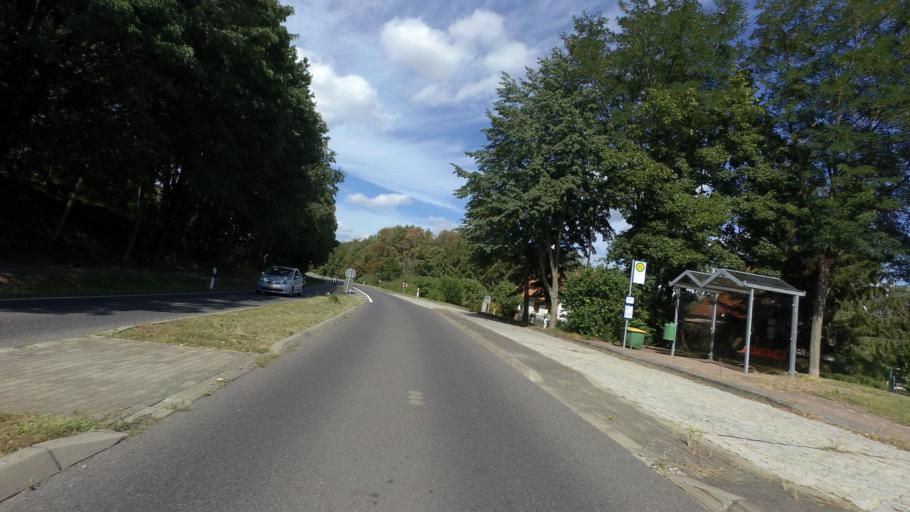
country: DE
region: Brandenburg
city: Wustermark
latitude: 52.5222
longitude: 12.9362
